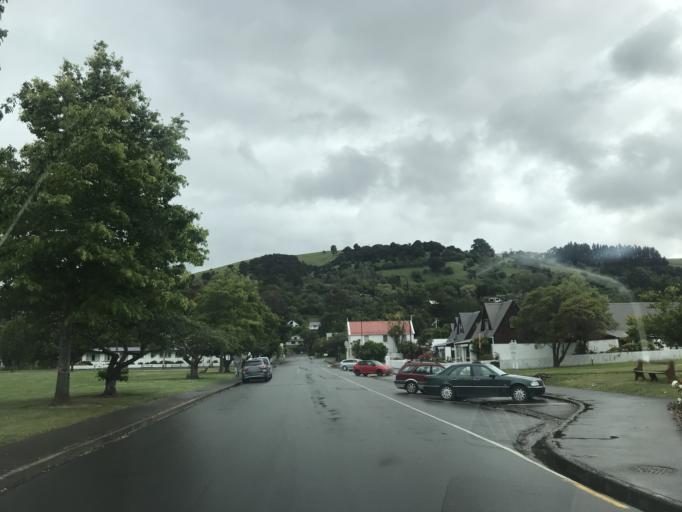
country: NZ
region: Canterbury
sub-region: Christchurch City
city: Christchurch
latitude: -43.8027
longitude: 172.9689
